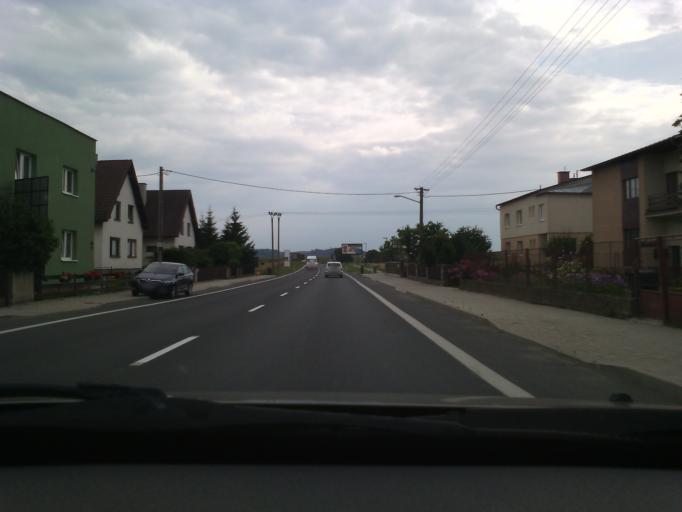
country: SK
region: Presovsky
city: Spisska Bela
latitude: 49.1831
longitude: 20.4522
